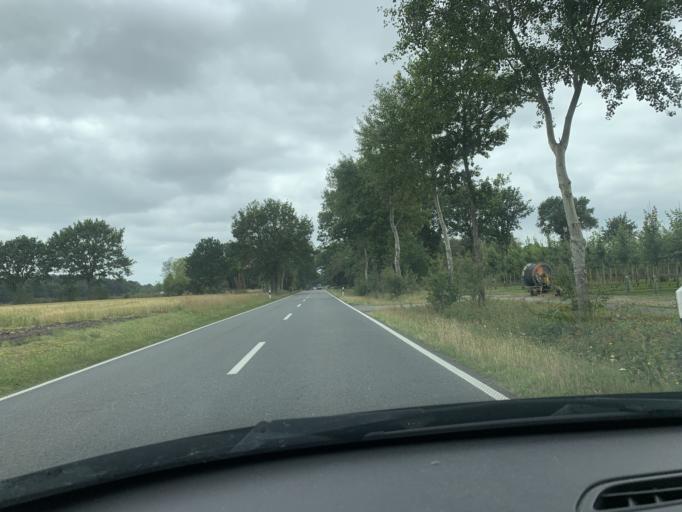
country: DE
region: Lower Saxony
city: Bad Zwischenahn
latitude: 53.2257
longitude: 7.9830
